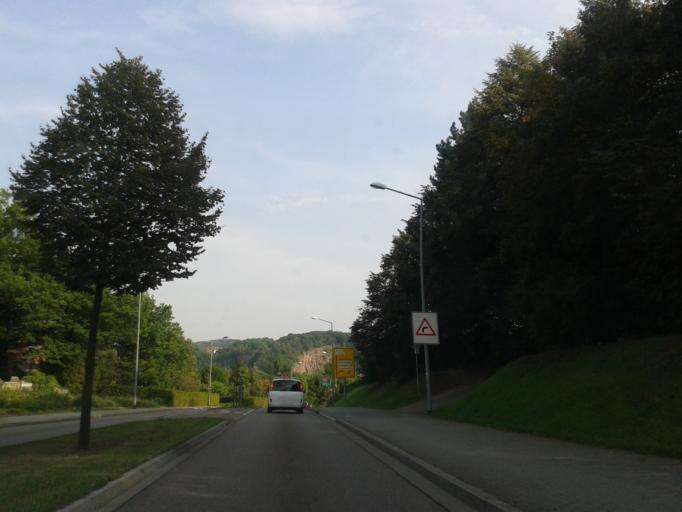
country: DE
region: Saxony
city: Freital
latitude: 51.0121
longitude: 13.6523
